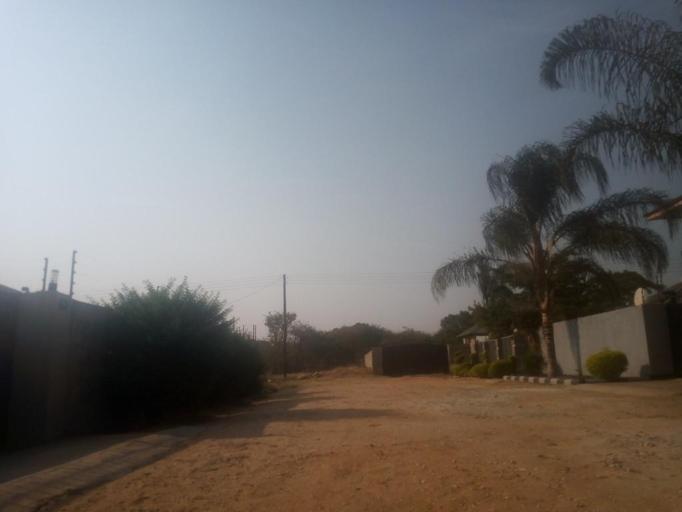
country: ZM
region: Lusaka
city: Lusaka
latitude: -15.4004
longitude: 28.3876
